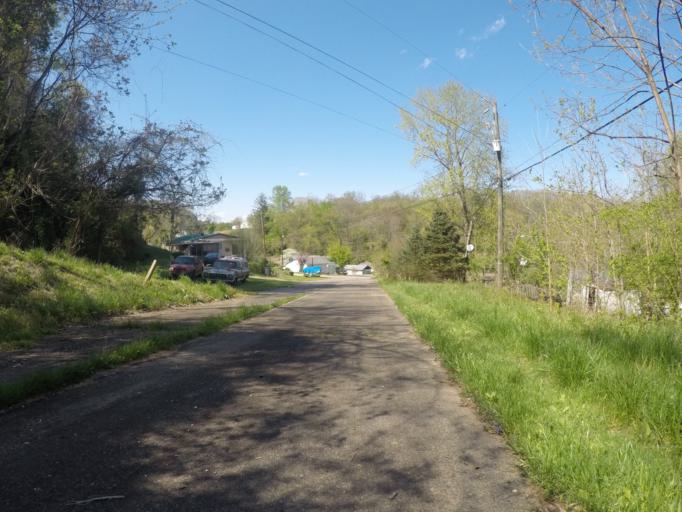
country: US
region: West Virginia
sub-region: Wayne County
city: Kenova
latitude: 38.3873
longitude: -82.5823
